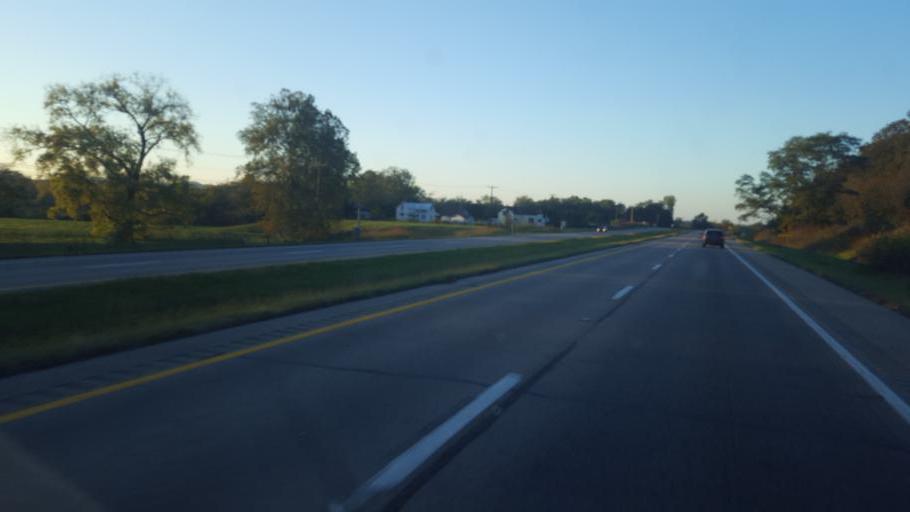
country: US
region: Ohio
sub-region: Scioto County
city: Lucasville
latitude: 38.9555
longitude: -83.0235
